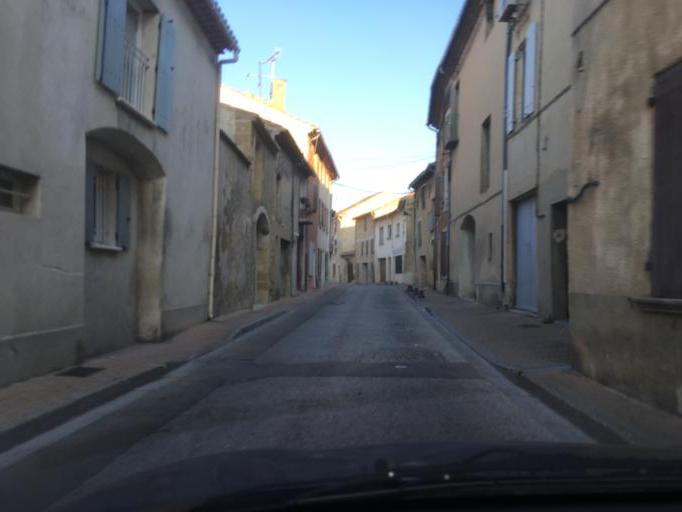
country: FR
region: Languedoc-Roussillon
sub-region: Departement du Gard
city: Roquemaure
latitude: 44.0512
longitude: 4.7779
